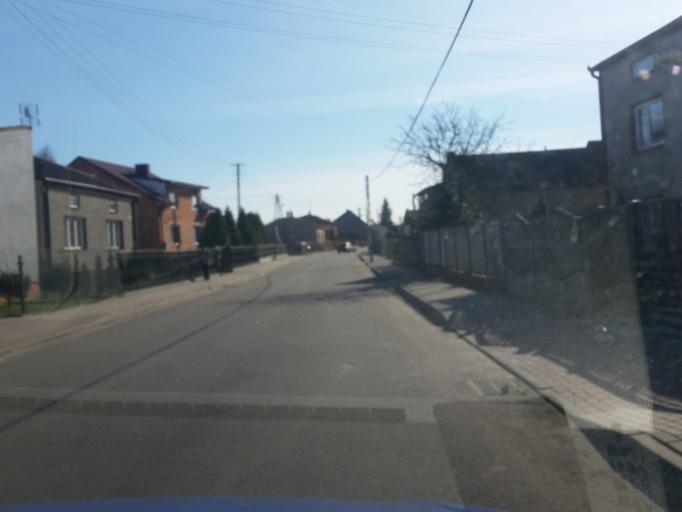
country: PL
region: Lodz Voivodeship
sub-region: Powiat piotrkowski
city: Gorzkowice
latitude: 51.2069
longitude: 19.5470
